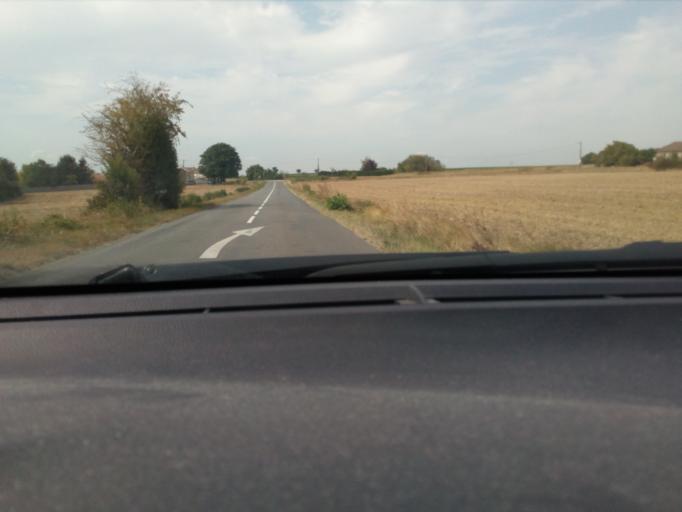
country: FR
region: Poitou-Charentes
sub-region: Departement de la Charente
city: Saint-Saturnin
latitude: 45.6692
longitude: 0.0281
